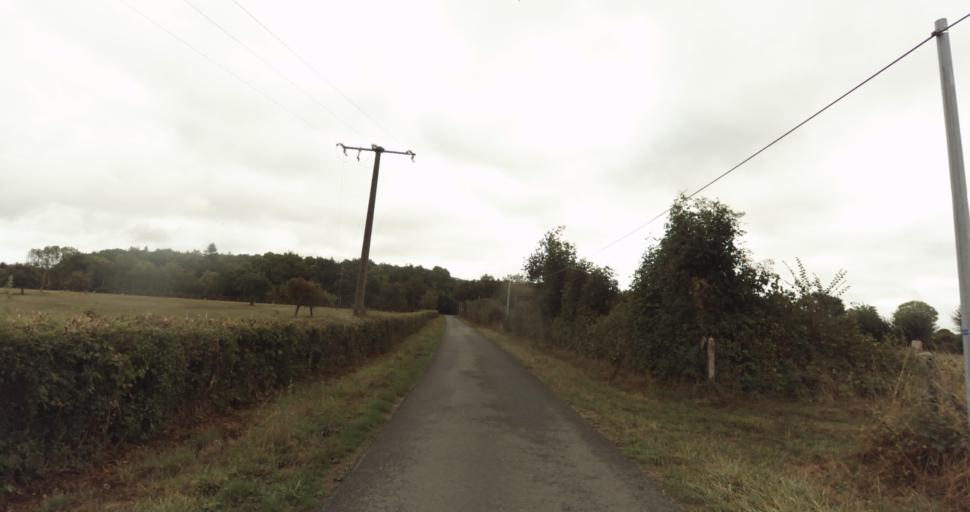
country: FR
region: Lower Normandy
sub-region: Departement de l'Orne
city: Gace
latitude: 48.8718
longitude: 0.3024
